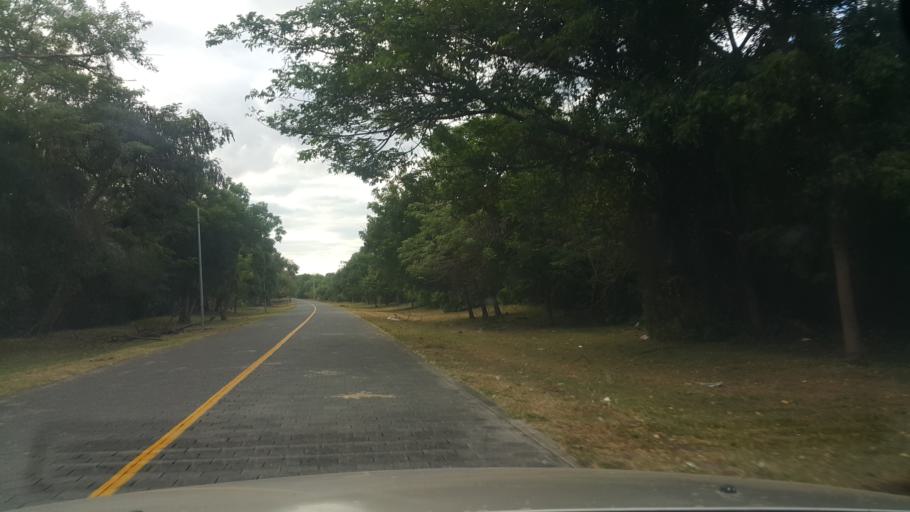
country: NI
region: Rivas
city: Moyogalpa
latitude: 11.4922
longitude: -85.6677
